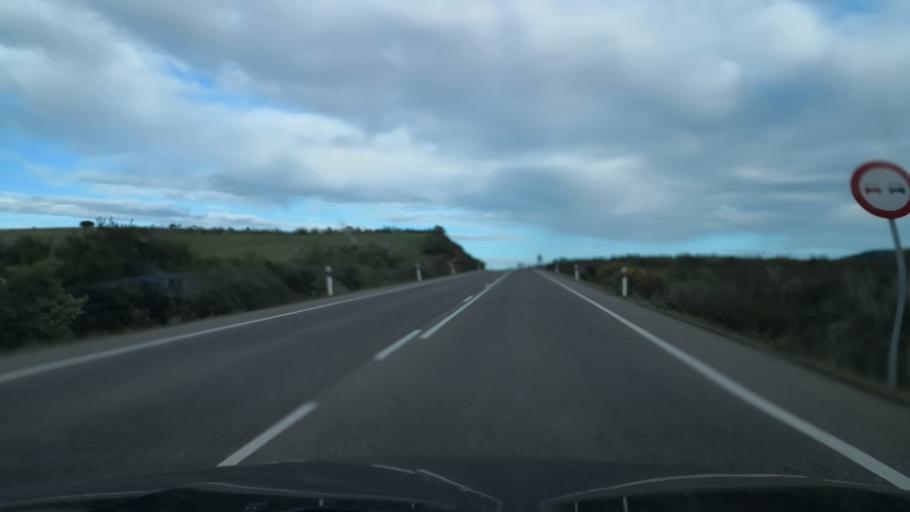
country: ES
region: Extremadura
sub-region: Provincia de Caceres
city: Pedroso de Acim
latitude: 39.8466
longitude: -6.4113
